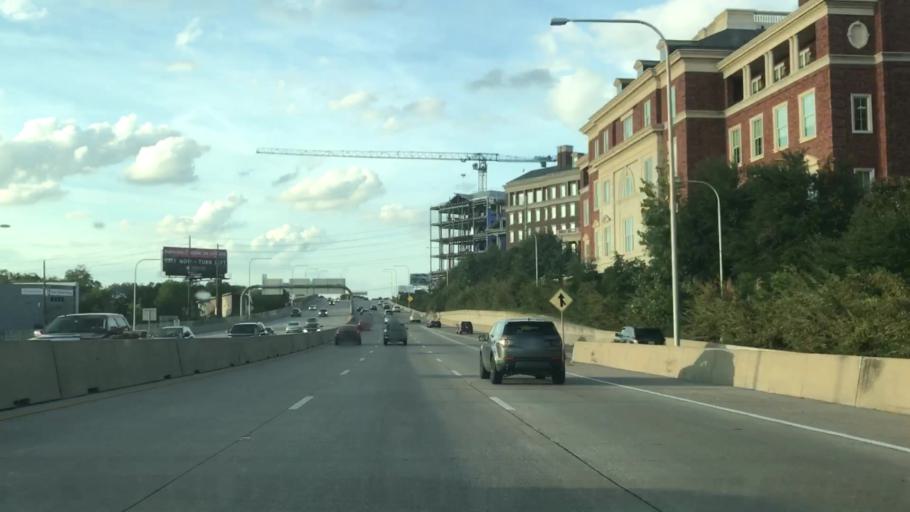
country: US
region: Texas
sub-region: Dallas County
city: Dallas
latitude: 32.8035
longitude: -96.8168
